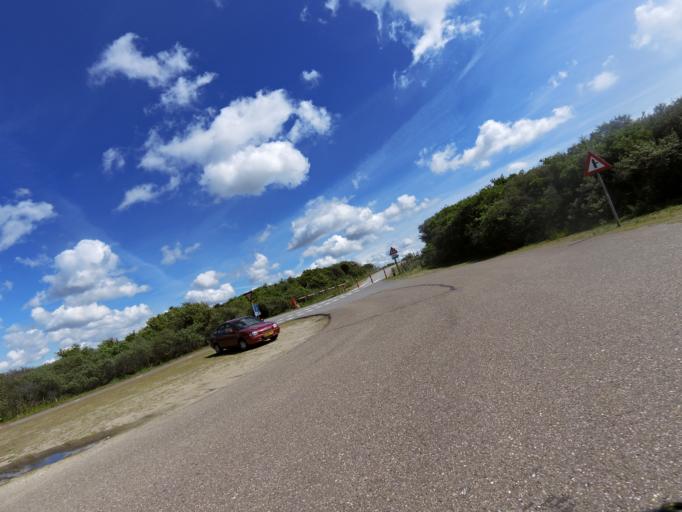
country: NL
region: South Holland
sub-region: Gemeente Rotterdam
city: Hoek van Holland
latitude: 51.9265
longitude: 4.0405
